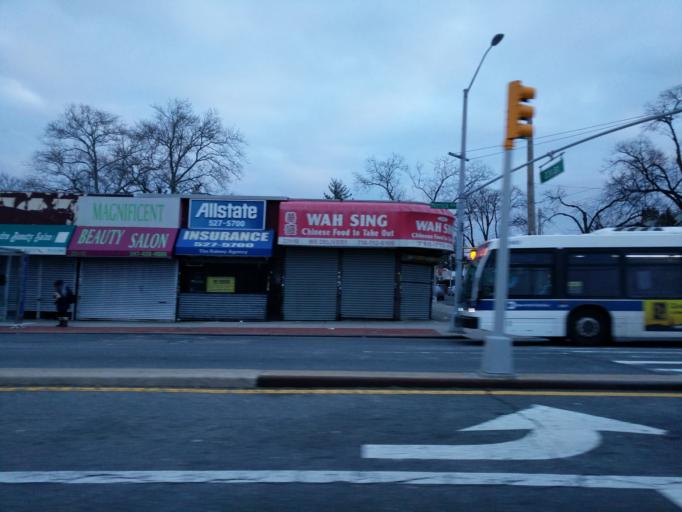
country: US
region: New York
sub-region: Nassau County
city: South Valley Stream
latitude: 40.6756
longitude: -73.7388
